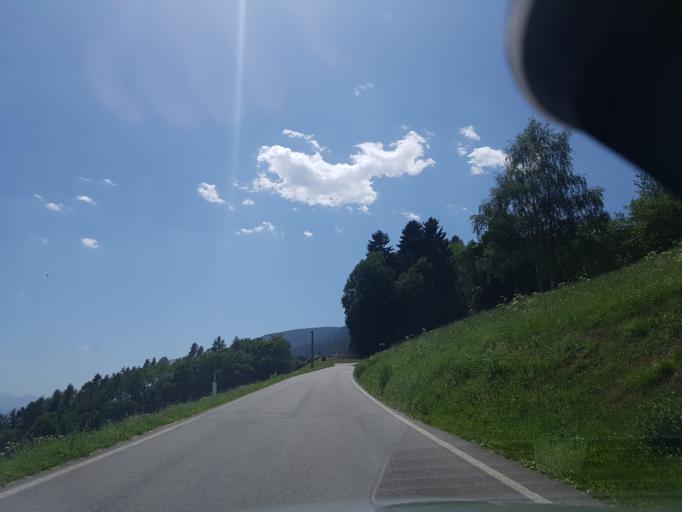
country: IT
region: Trentino-Alto Adige
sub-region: Bolzano
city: Villandro - Villanders
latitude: 46.6296
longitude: 11.5276
